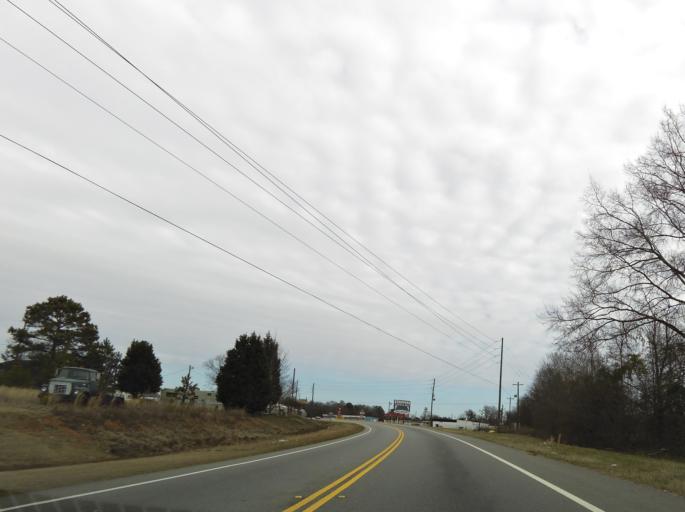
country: US
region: Georgia
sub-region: Peach County
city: Byron
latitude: 32.6065
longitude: -83.7530
